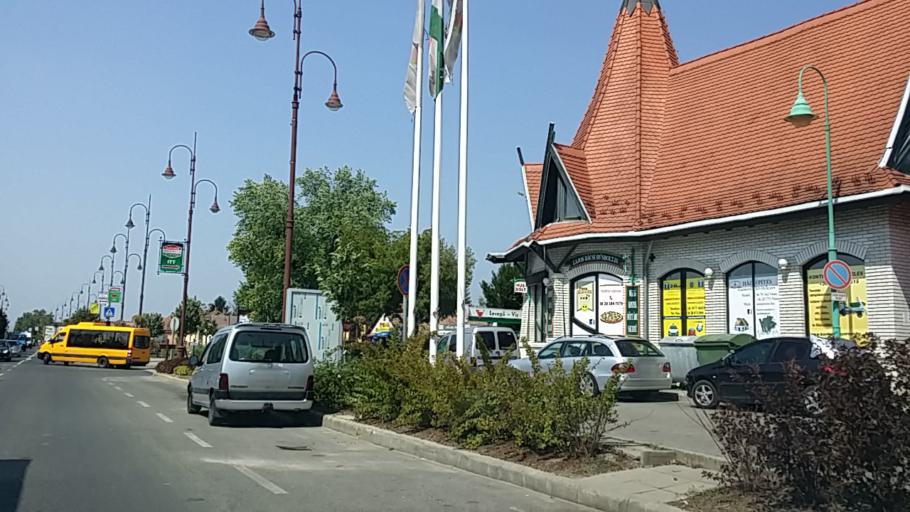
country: HU
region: Pest
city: Veresegyhaz
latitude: 47.6542
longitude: 19.2881
